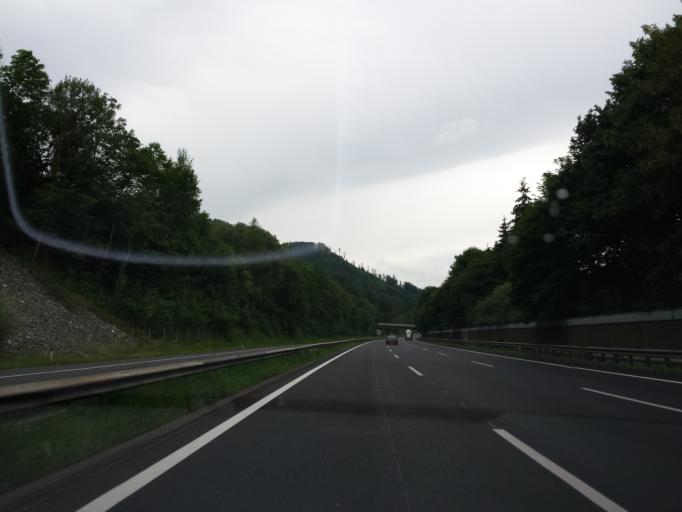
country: AT
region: Styria
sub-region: Politischer Bezirk Graz-Umgebung
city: Ubelbach
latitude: 47.2173
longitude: 15.2544
